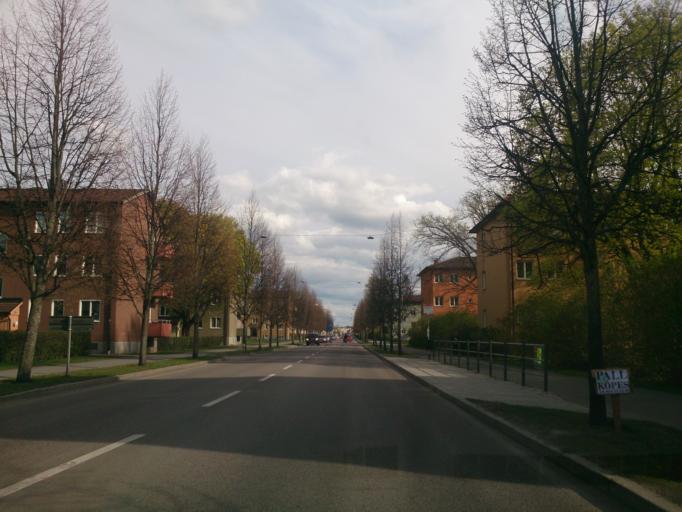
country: SE
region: OEstergoetland
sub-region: Linkopings Kommun
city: Linkoping
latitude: 58.4101
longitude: 15.6364
